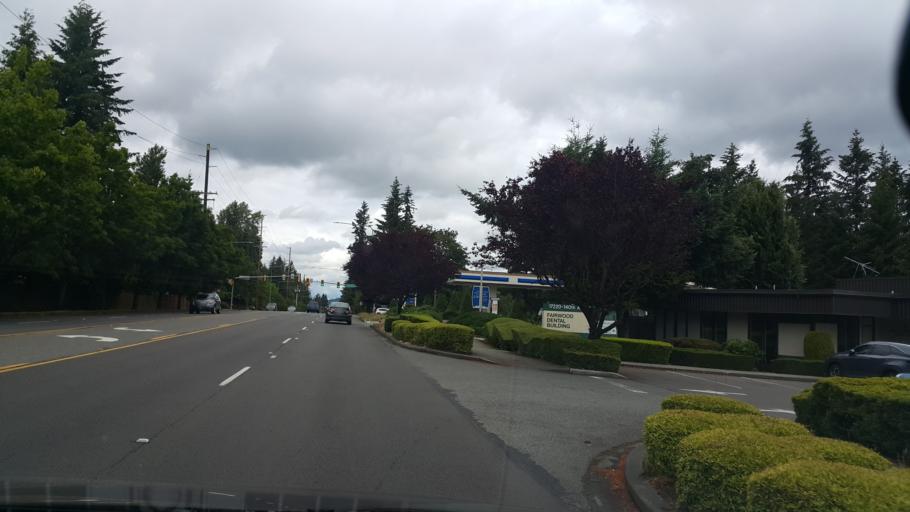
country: US
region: Washington
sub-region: King County
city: Fairwood
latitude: 47.4479
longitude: -122.1540
